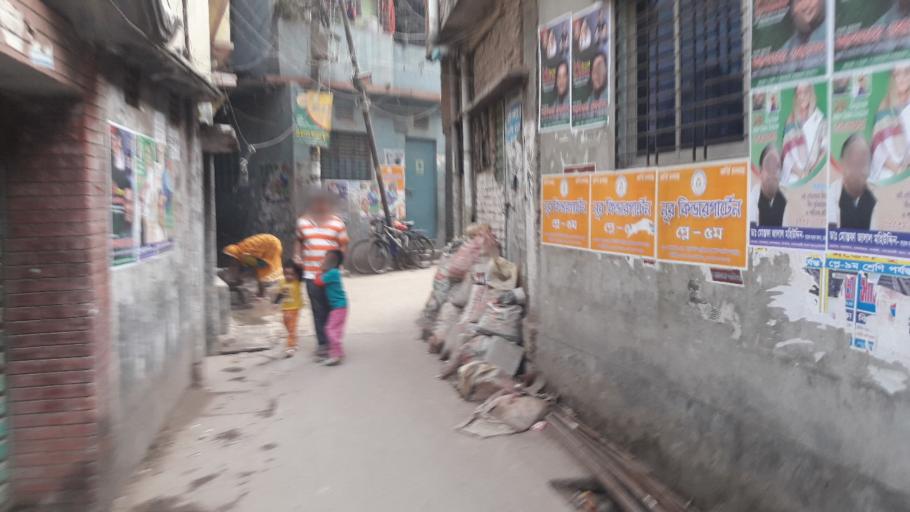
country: BD
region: Dhaka
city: Azimpur
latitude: 23.7219
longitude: 90.3777
